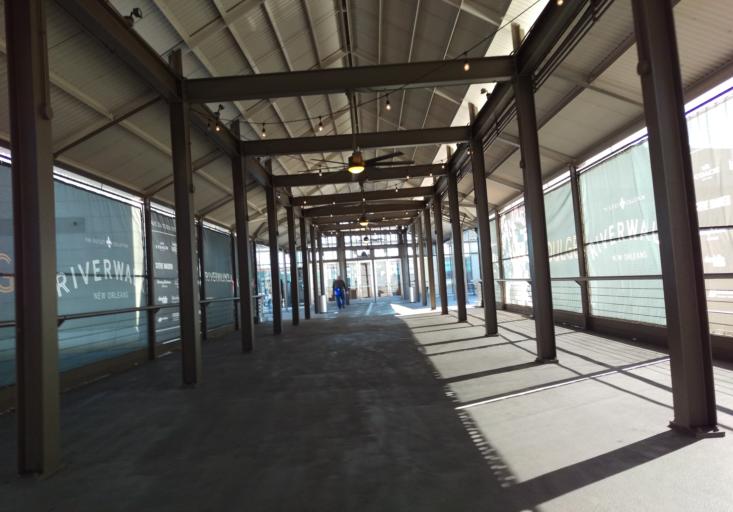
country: US
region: Louisiana
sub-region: Orleans Parish
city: New Orleans
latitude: 29.9439
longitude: -90.0627
